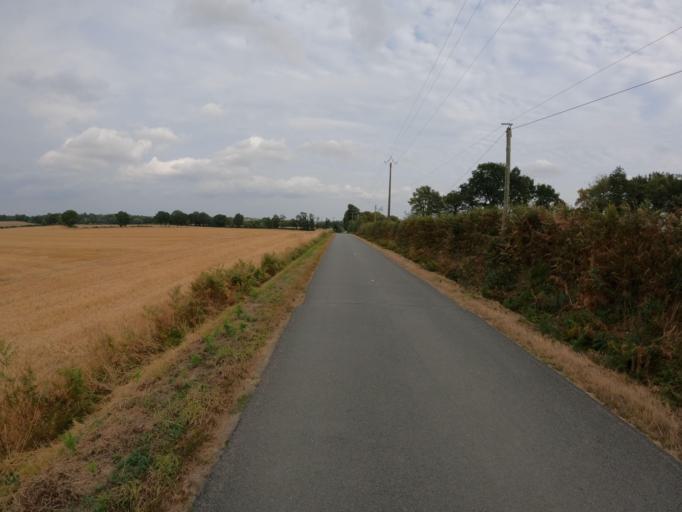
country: FR
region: Pays de la Loire
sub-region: Departement de Maine-et-Loire
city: La Romagne
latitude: 47.0510
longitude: -1.0040
